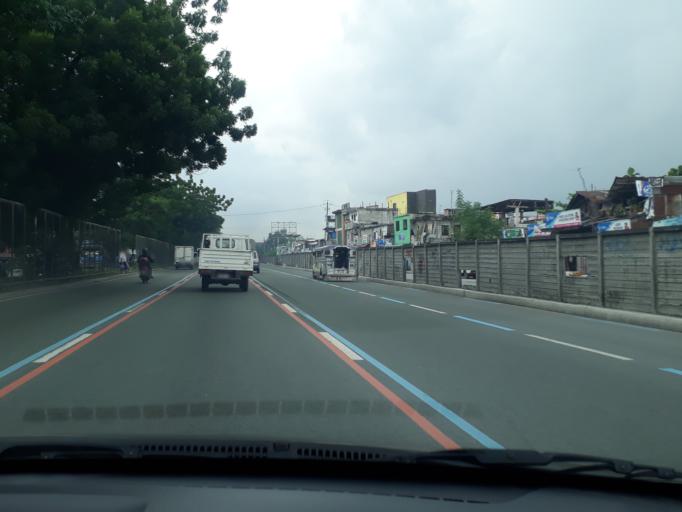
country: PH
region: Calabarzon
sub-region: Province of Rizal
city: Pateros
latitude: 14.5257
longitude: 121.0556
